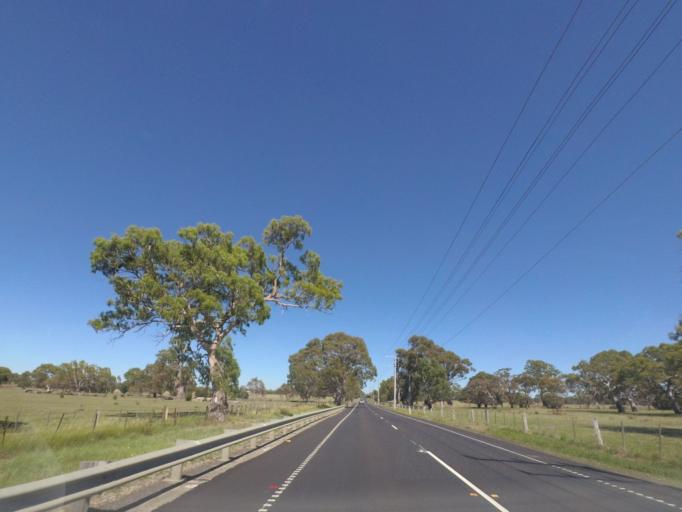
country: AU
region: Victoria
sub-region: Whittlesea
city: Mernda
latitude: -37.5530
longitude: 145.0664
